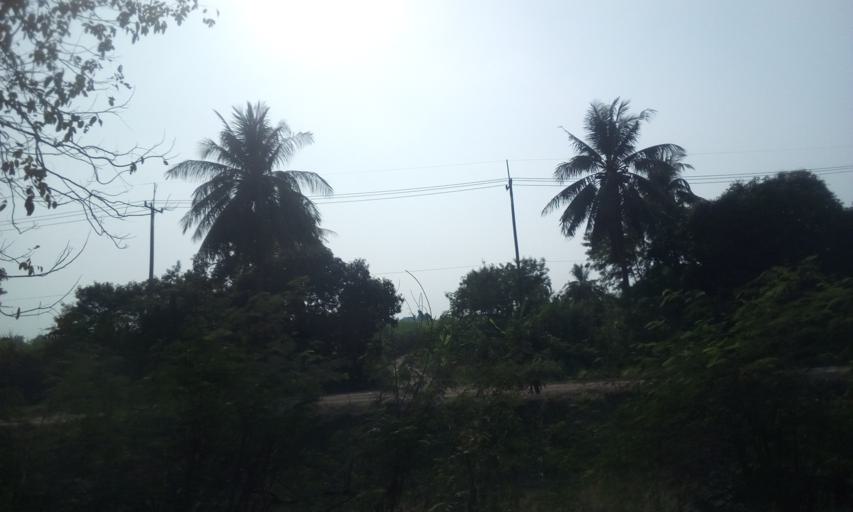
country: TH
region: Sing Buri
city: Phrom Buri
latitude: 14.7496
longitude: 100.4409
